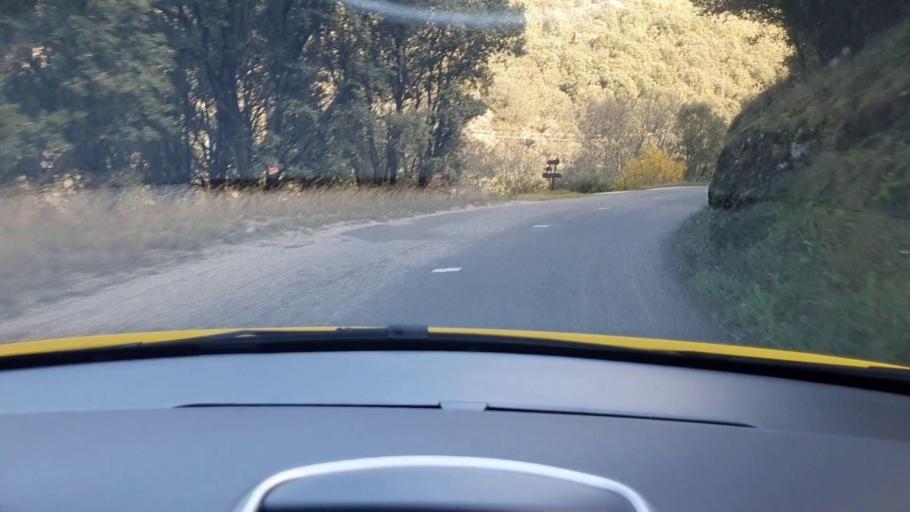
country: FR
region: Languedoc-Roussillon
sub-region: Departement du Gard
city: Valleraugue
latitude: 44.1633
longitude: 3.6665
